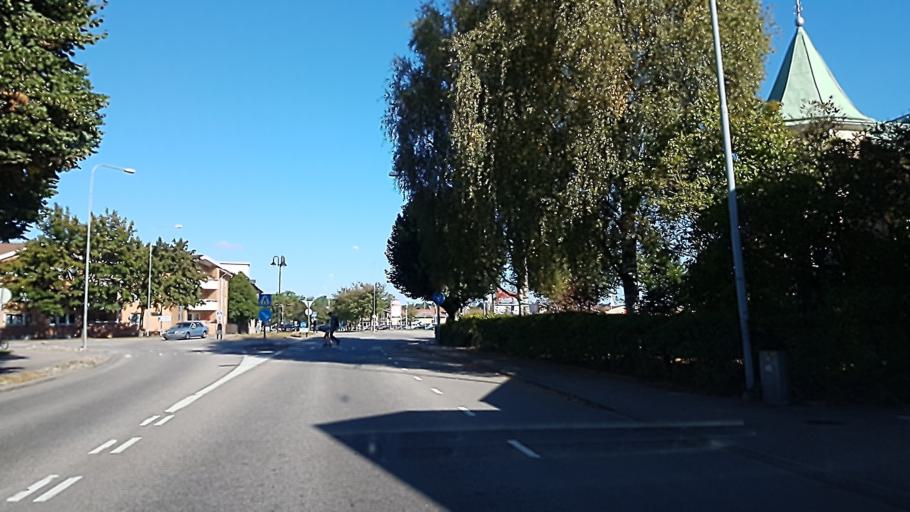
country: SE
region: Kronoberg
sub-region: Ljungby Kommun
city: Ljungby
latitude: 56.8326
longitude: 13.9441
